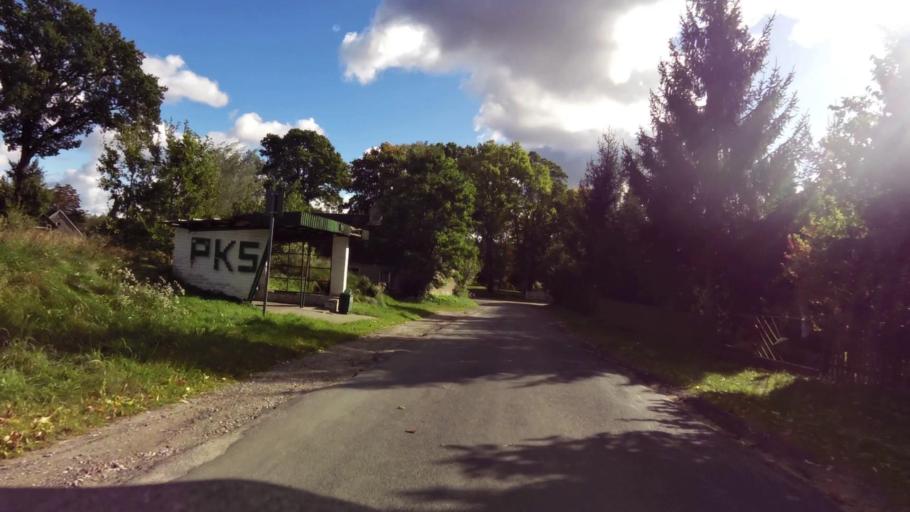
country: PL
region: West Pomeranian Voivodeship
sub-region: Powiat bialogardzki
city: Bialogard
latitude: 53.9925
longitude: 16.0667
